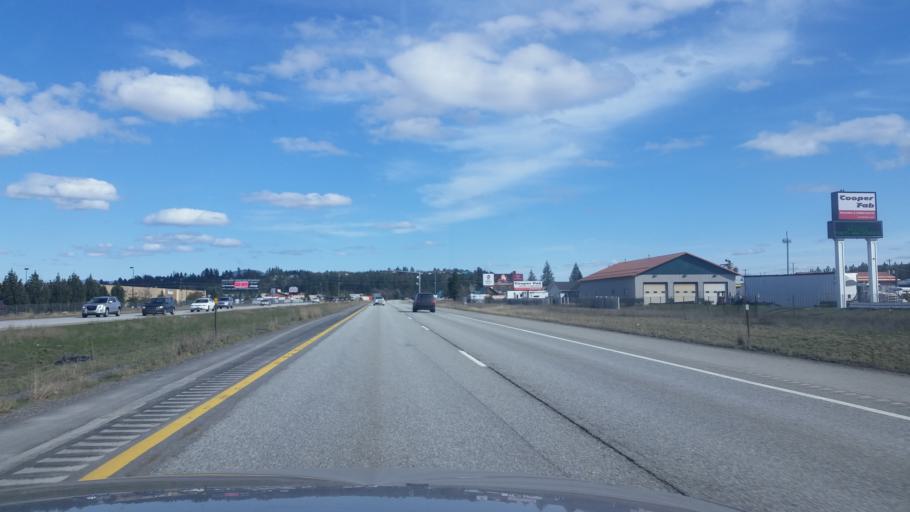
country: US
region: Idaho
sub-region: Kootenai County
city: Post Falls
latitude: 47.7125
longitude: -116.9115
